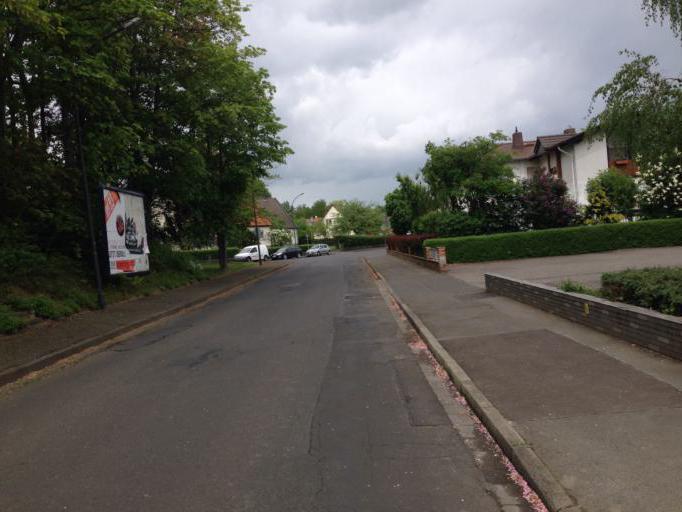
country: DE
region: Hesse
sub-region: Regierungsbezirk Giessen
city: Alsfeld
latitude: 50.7467
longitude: 9.2590
